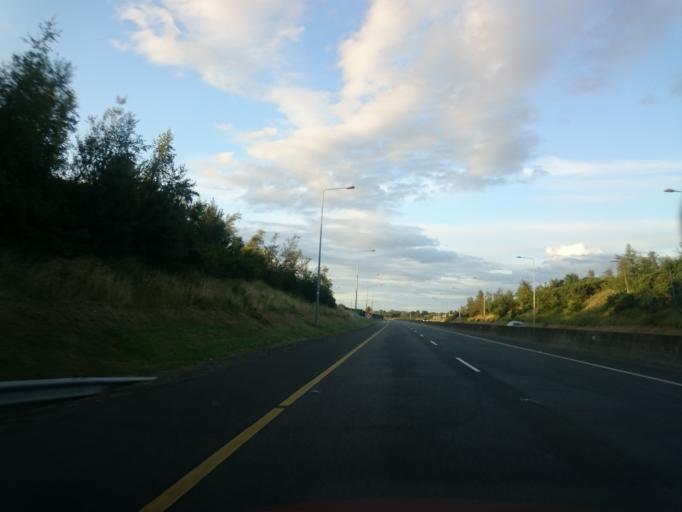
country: IE
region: Leinster
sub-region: Loch Garman
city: Gorey
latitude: 52.7117
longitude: -6.2559
